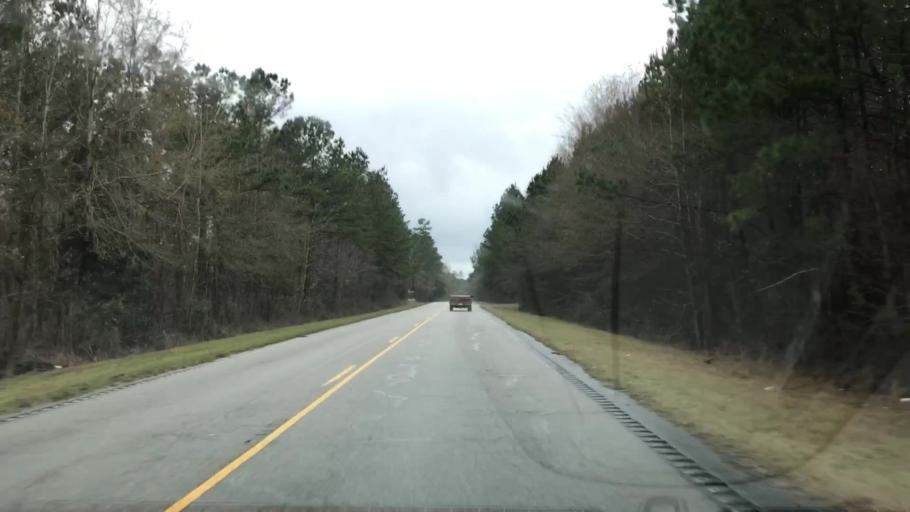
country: US
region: South Carolina
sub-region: Williamsburg County
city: Andrews
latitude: 33.5265
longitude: -79.4897
